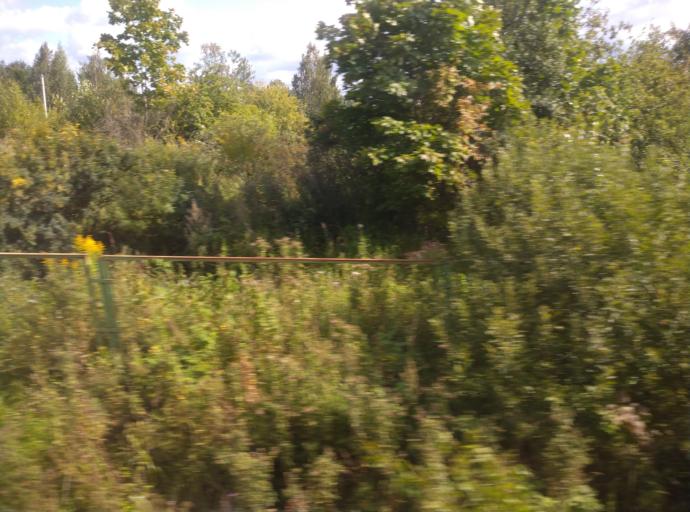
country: RU
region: Leningrad
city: Krasnyy Bor
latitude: 59.6830
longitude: 30.6976
